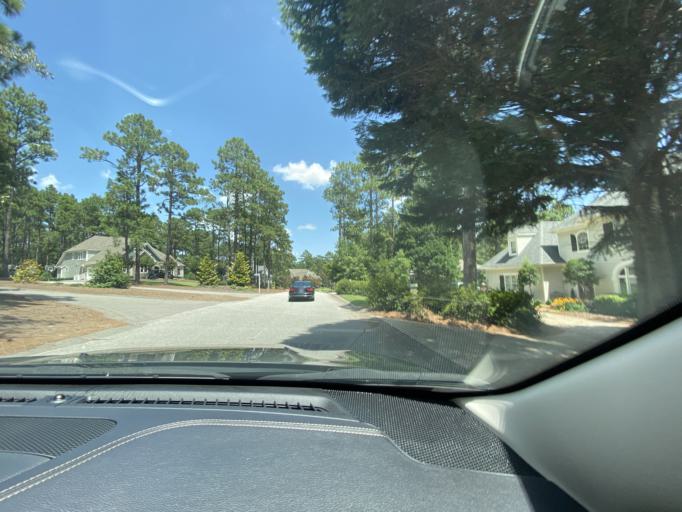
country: US
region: North Carolina
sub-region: Moore County
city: Pinehurst
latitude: 35.1977
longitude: -79.4356
